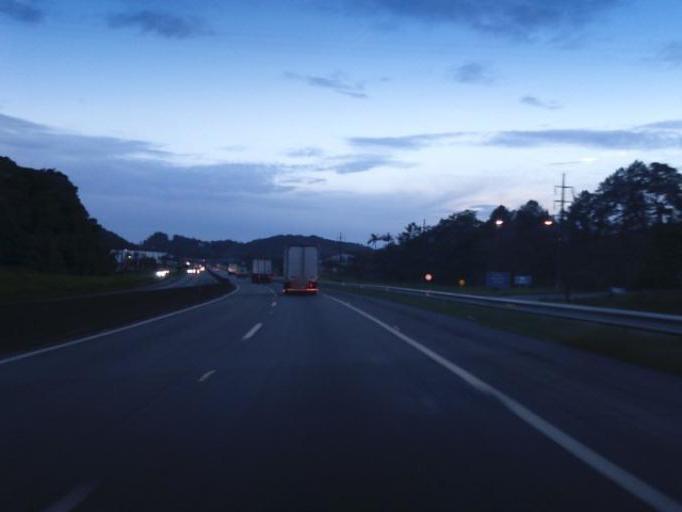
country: BR
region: Santa Catarina
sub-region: Joinville
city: Joinville
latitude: -26.3025
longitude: -48.8829
